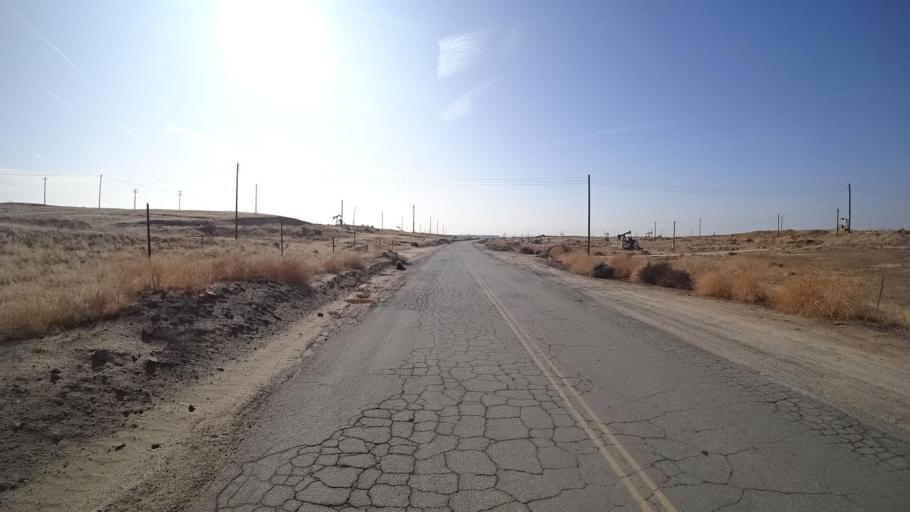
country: US
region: California
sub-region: Kern County
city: Oildale
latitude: 35.4677
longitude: -119.0485
